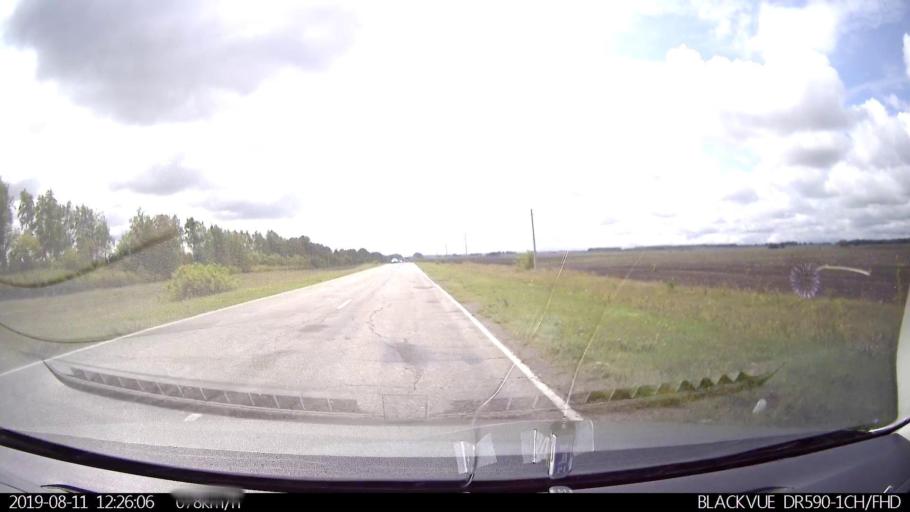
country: RU
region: Ulyanovsk
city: Ignatovka
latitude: 53.8672
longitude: 47.9336
